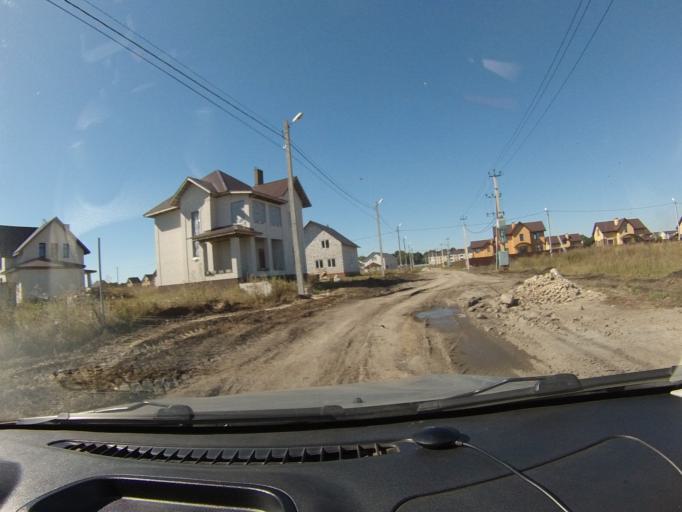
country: RU
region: Tambov
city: Komsomolets
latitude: 52.7812
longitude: 41.3686
